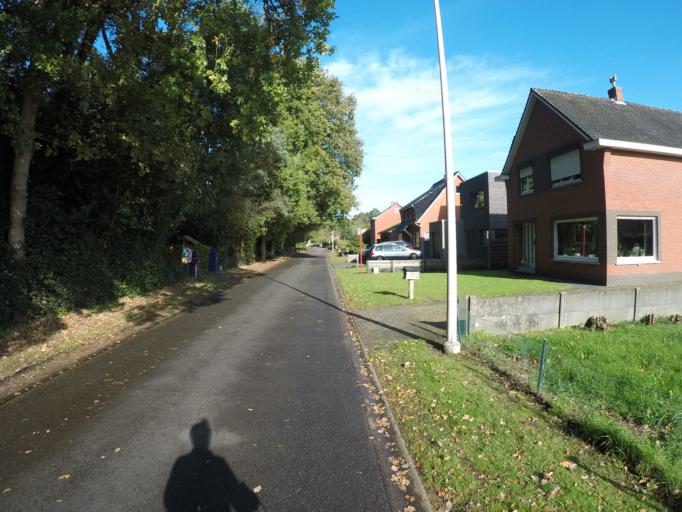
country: BE
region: Flanders
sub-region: Provincie Antwerpen
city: Zoersel
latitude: 51.2701
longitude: 4.7065
